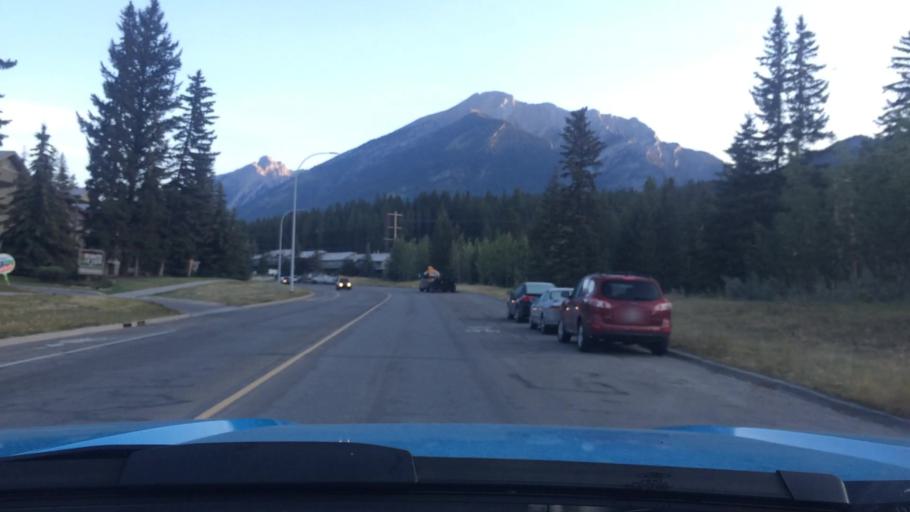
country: CA
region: Alberta
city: Canmore
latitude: 51.0796
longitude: -115.3212
